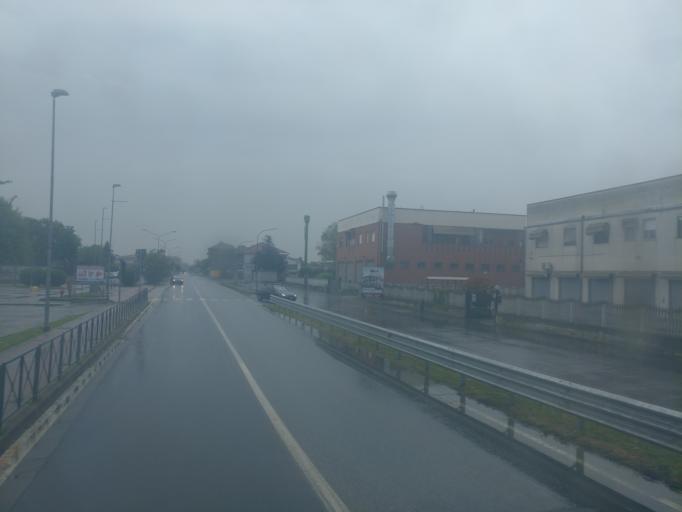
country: IT
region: Piedmont
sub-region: Provincia di Torino
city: La Loggia
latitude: 44.9464
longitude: 7.6696
